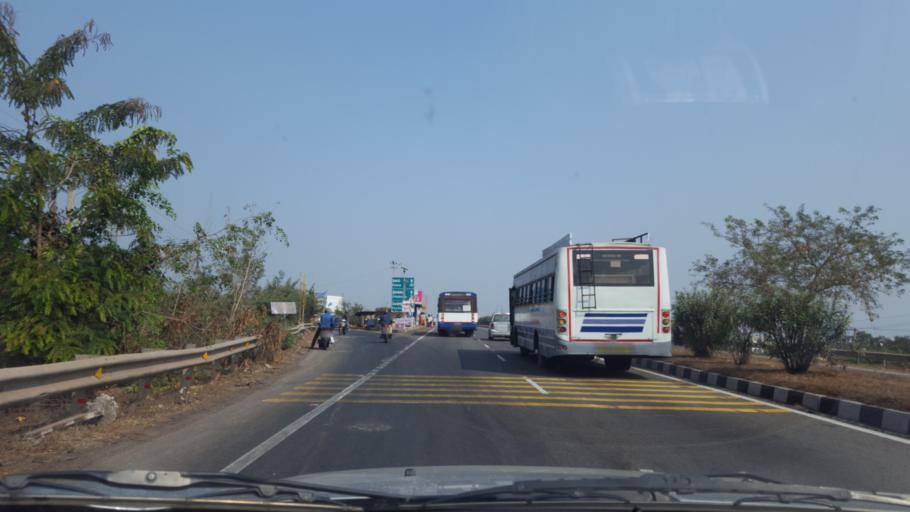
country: IN
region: Andhra Pradesh
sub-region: Vishakhapatnam
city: Bhimunipatnam
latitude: 17.8925
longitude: 83.3780
